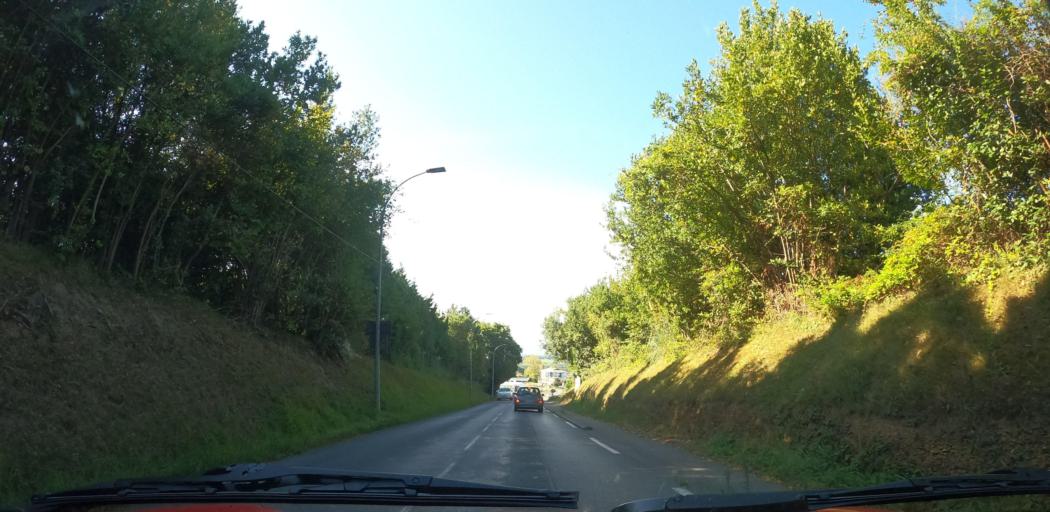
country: FR
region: Aquitaine
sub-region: Departement des Pyrenees-Atlantiques
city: Arbonne
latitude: 43.4486
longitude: -1.5443
